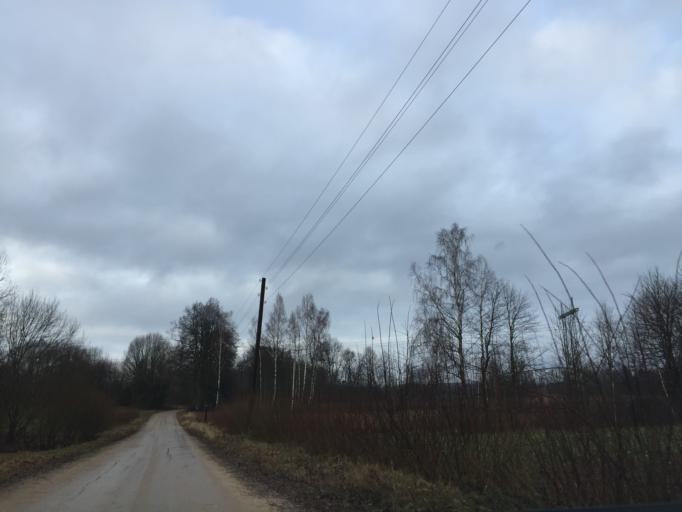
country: LV
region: Vainode
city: Vainode
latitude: 56.6121
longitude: 21.7960
